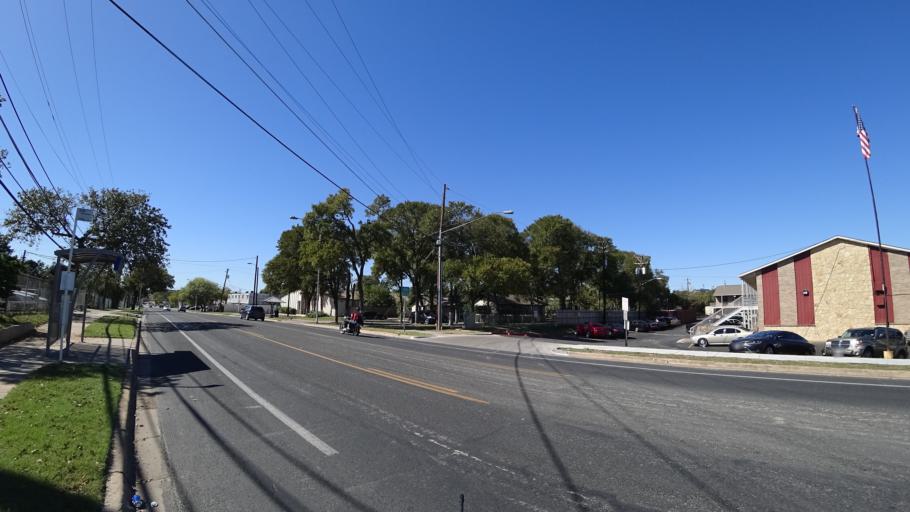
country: US
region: Texas
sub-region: Travis County
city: Austin
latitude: 30.2868
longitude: -97.7026
